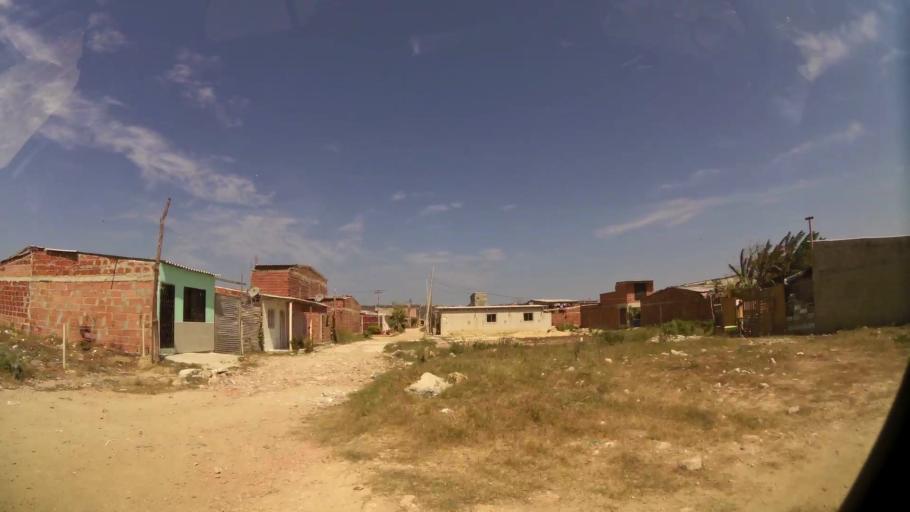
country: CO
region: Atlantico
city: Barranquilla
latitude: 10.9754
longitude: -74.8490
